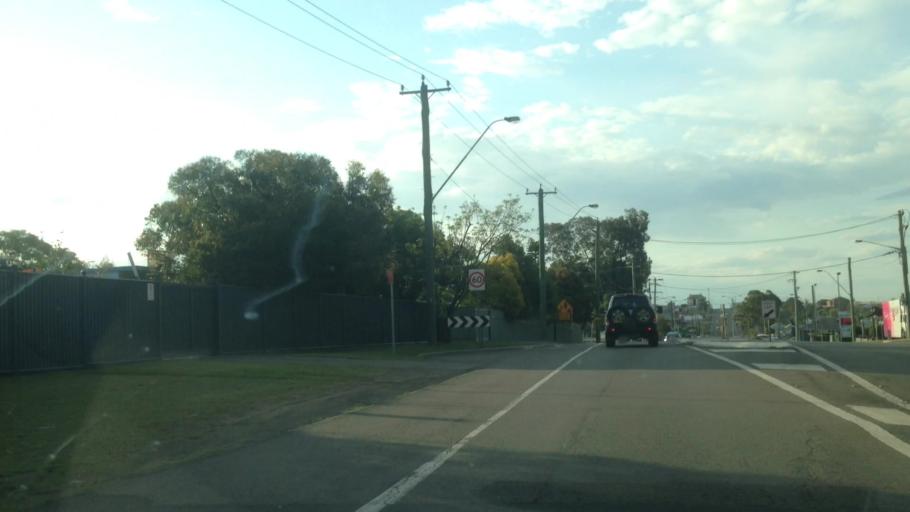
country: AU
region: New South Wales
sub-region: Cessnock
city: Kurri Kurri
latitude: -32.8266
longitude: 151.4875
